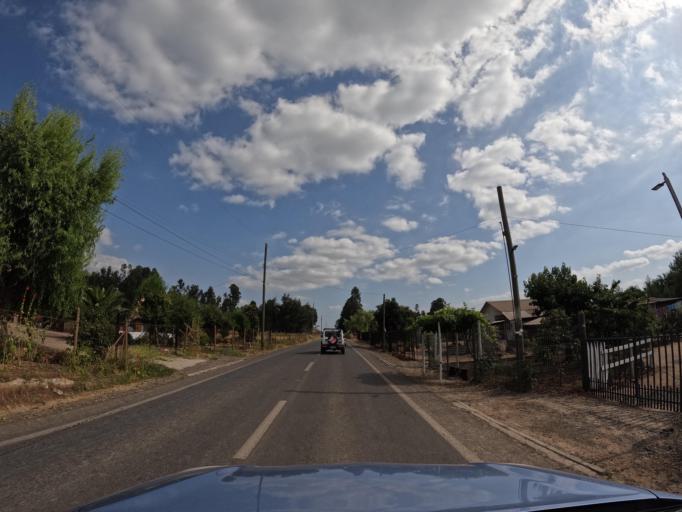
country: CL
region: Maule
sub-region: Provincia de Curico
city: Molina
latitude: -35.1993
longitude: -71.2973
